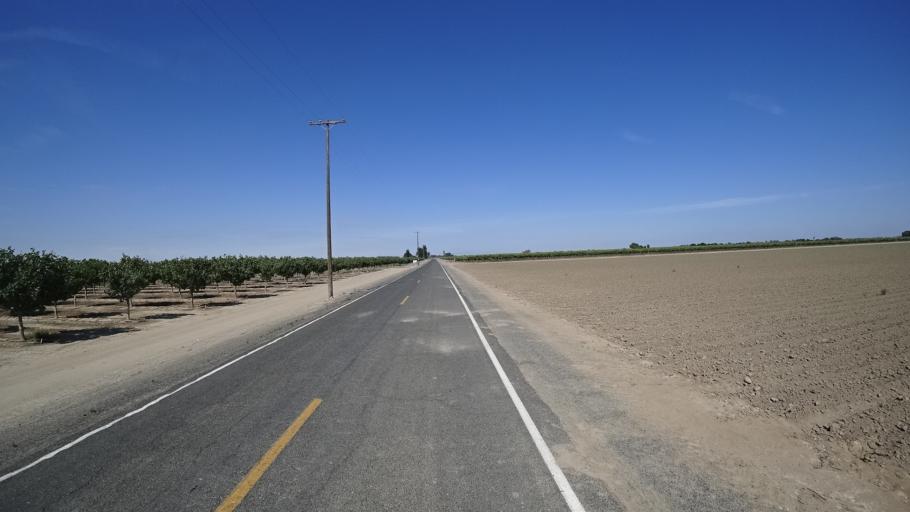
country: US
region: California
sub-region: Kings County
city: Armona
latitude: 36.2548
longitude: -119.7341
